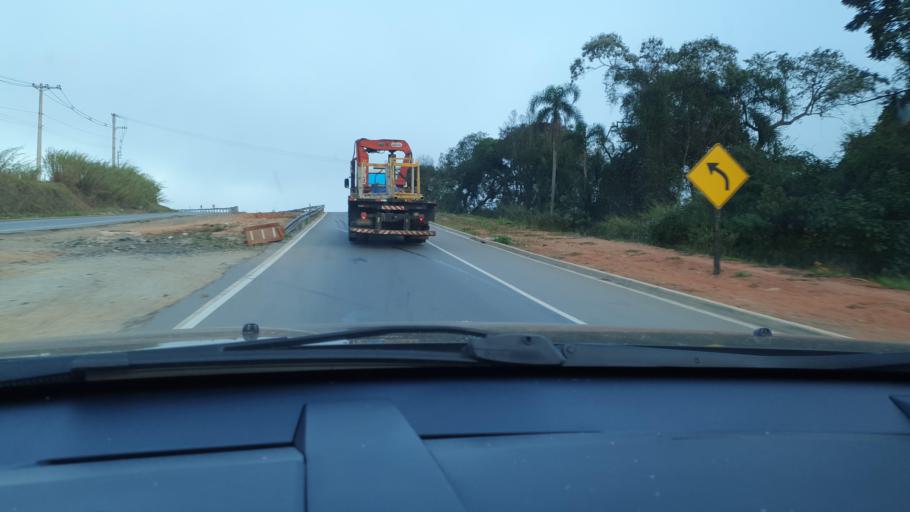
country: BR
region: Sao Paulo
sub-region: Vargem Grande Paulista
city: Vargem Grande Paulista
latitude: -23.6493
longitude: -47.0651
